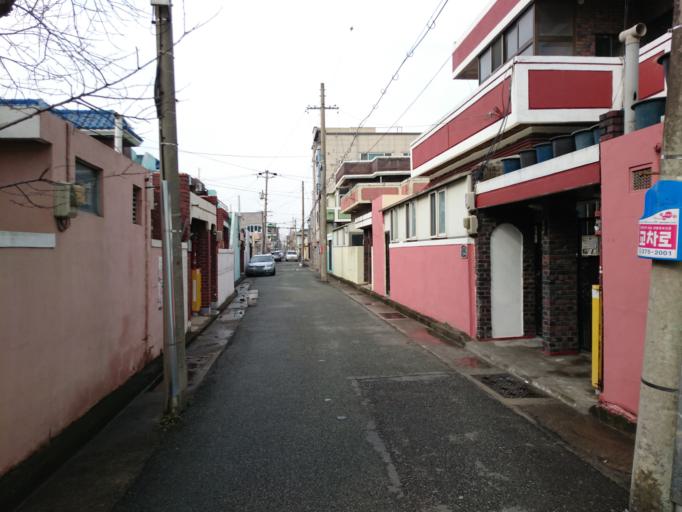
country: KR
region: Gyeongsangbuk-do
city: Pohang
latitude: 36.0242
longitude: 129.3736
